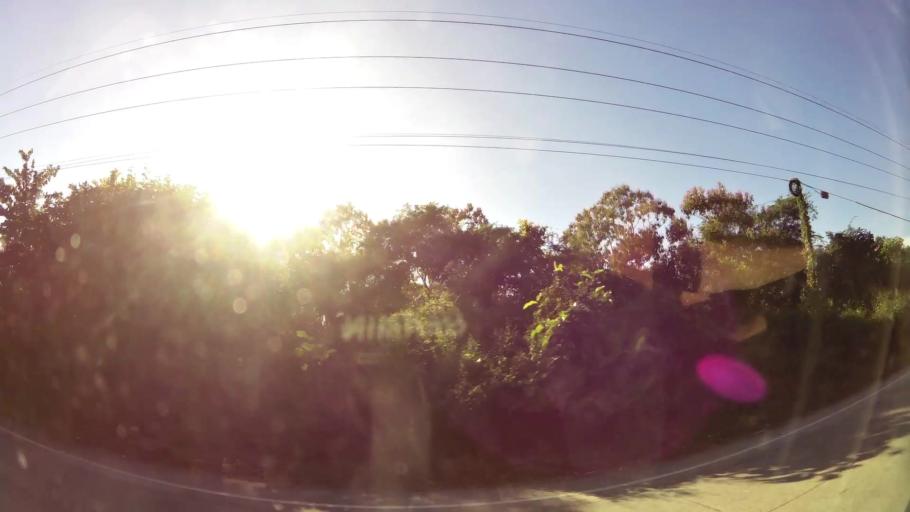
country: SV
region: Santa Ana
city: Metapan
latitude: 14.2640
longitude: -89.4597
